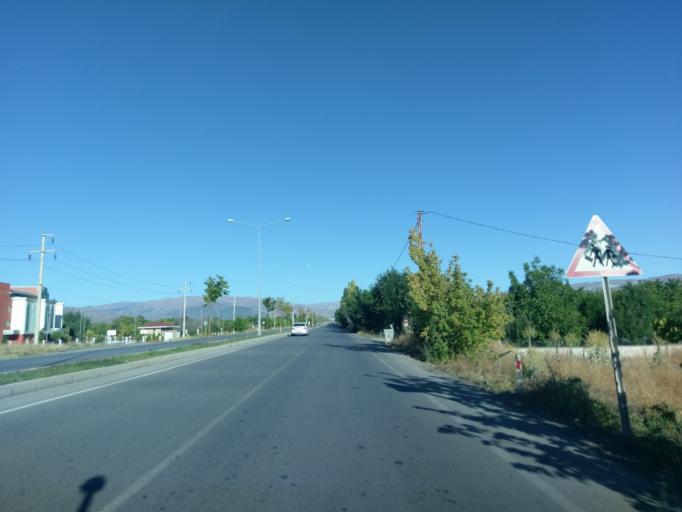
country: TR
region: Erzincan
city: Erzincan
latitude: 39.7683
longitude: 39.4296
